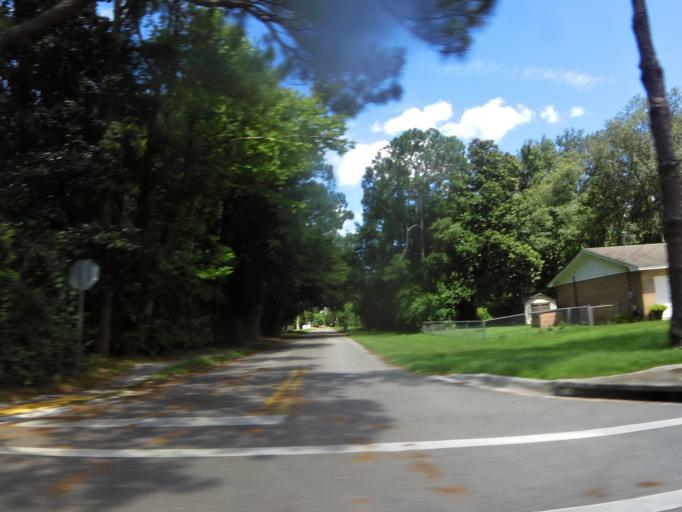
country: US
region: Florida
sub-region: Nassau County
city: Fernandina Beach
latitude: 30.6623
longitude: -81.4525
